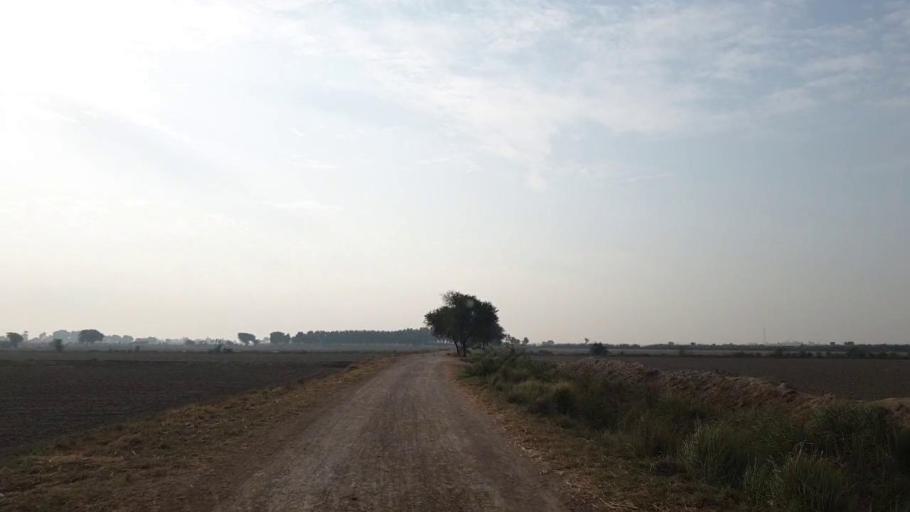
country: PK
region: Sindh
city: Tando Muhammad Khan
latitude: 25.1108
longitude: 68.4348
